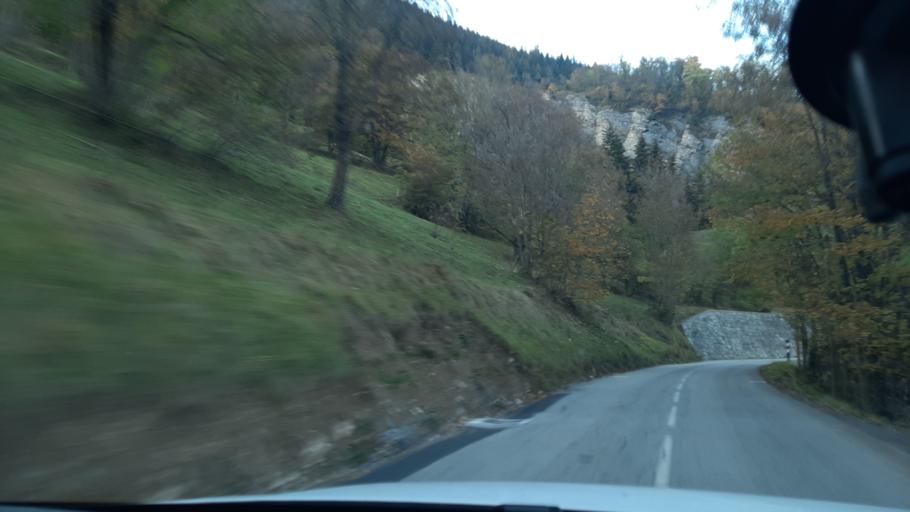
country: FR
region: Rhone-Alpes
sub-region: Departement de la Savoie
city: Saint-Jean-de-Maurienne
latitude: 45.2004
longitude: 6.3023
